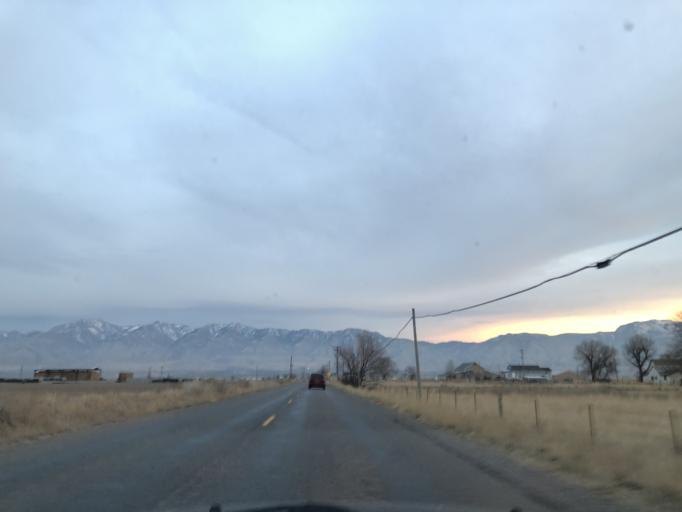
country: US
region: Utah
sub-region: Cache County
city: Benson
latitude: 41.7947
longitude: -111.8960
